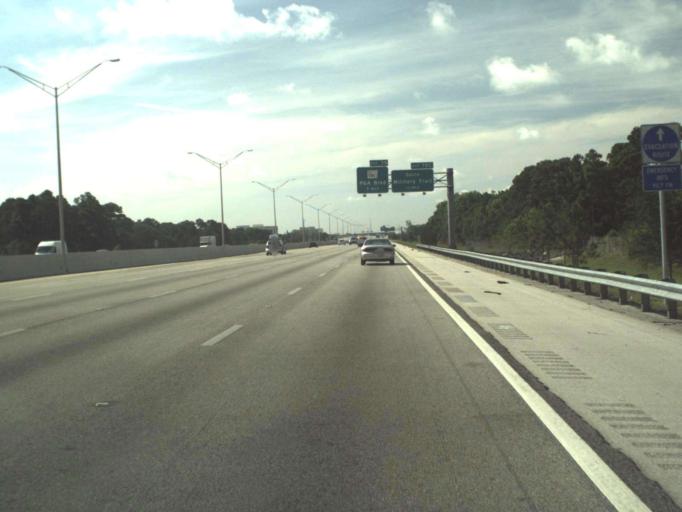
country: US
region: Florida
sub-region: Palm Beach County
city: Palm Beach Gardens
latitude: 26.8549
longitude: -80.1121
